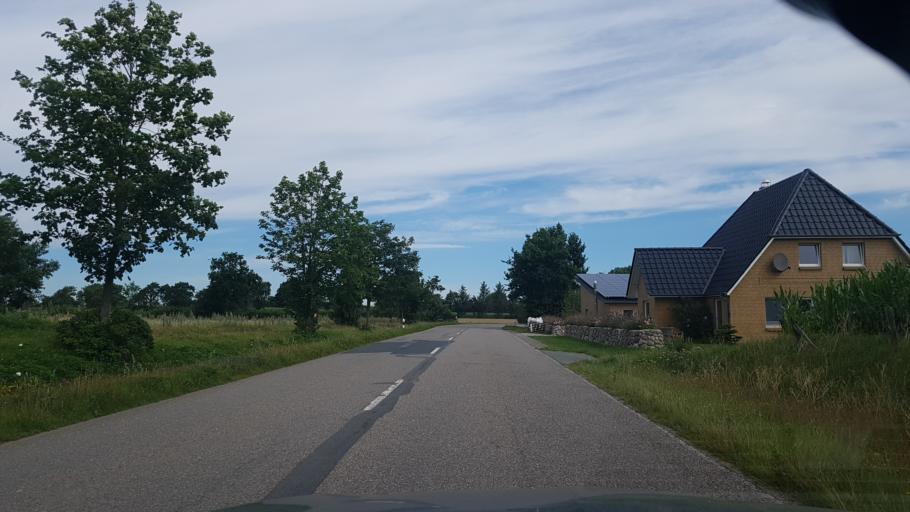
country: DE
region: Schleswig-Holstein
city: Ladelund
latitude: 54.8439
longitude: 9.0347
